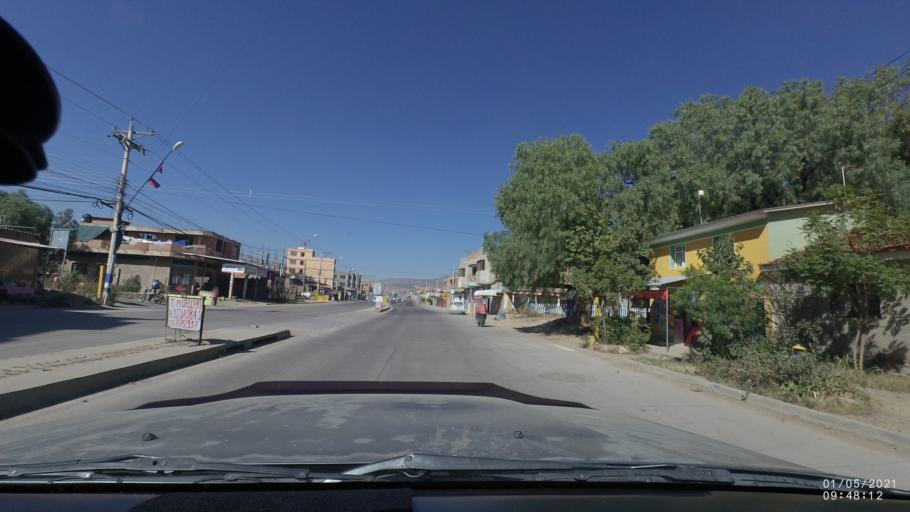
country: BO
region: Cochabamba
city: Cochabamba
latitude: -17.4518
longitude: -66.1665
